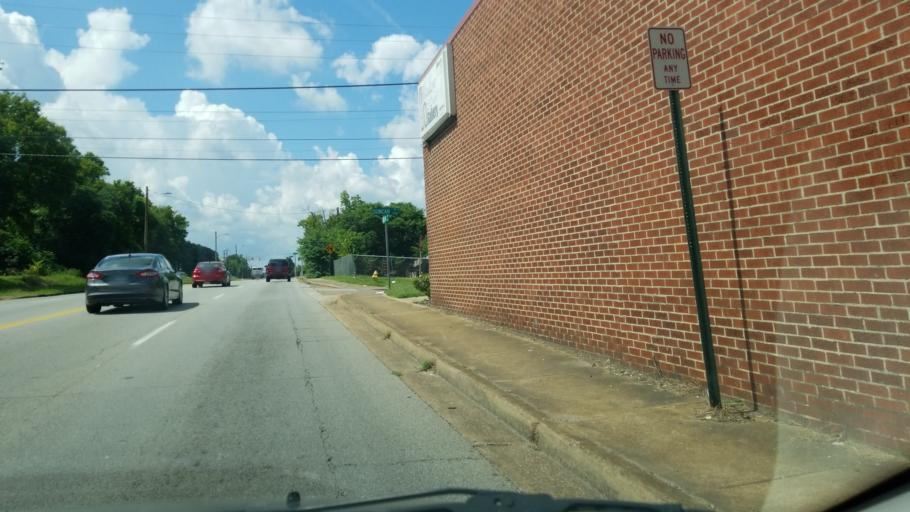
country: US
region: Tennessee
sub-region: Hamilton County
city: Chattanooga
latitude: 35.0384
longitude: -85.2832
